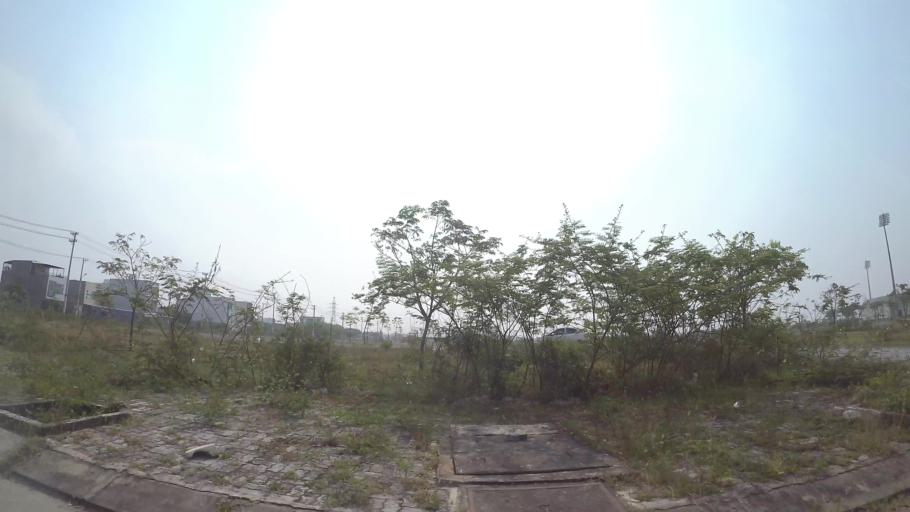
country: VN
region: Da Nang
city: Cam Le
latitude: 16.0019
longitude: 108.2235
